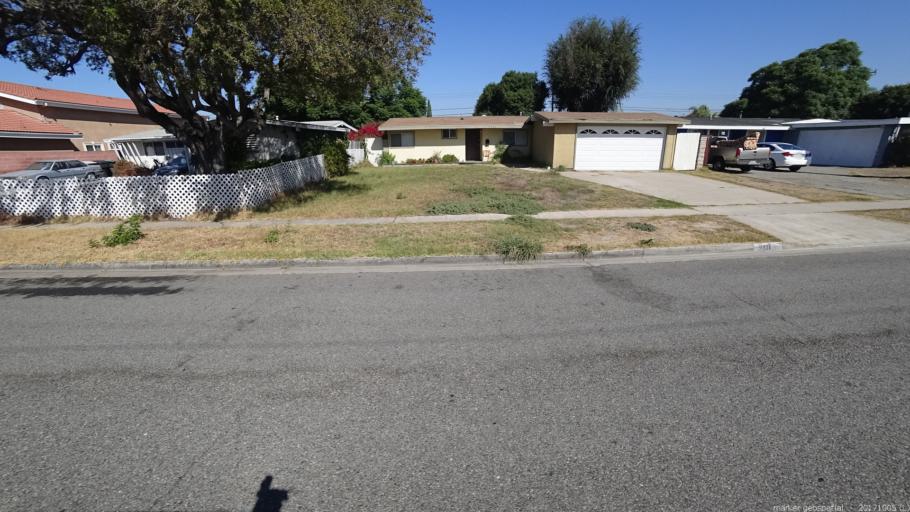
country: US
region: California
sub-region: Orange County
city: Stanton
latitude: 33.7981
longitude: -117.9702
